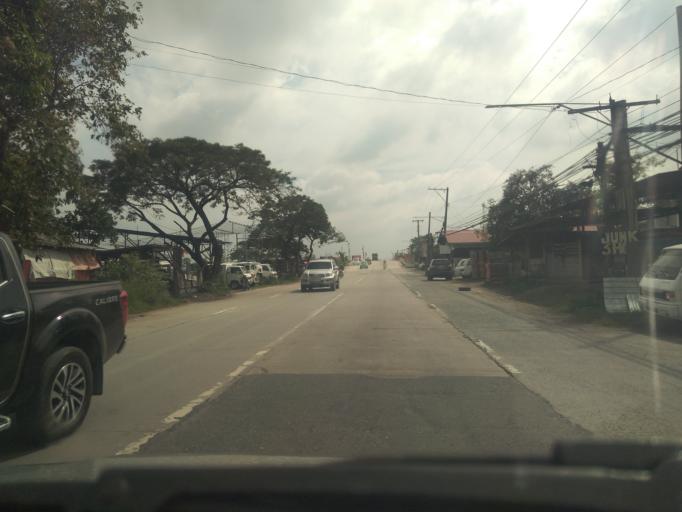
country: PH
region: Central Luzon
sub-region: Province of Pampanga
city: Santo Domingo
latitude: 15.0004
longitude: 120.7281
